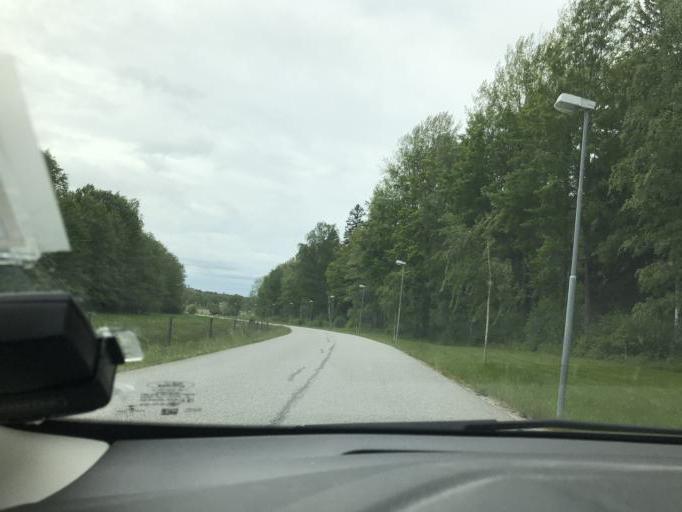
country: SE
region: Stockholm
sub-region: Botkyrka Kommun
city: Alby
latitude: 59.2191
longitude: 17.8438
